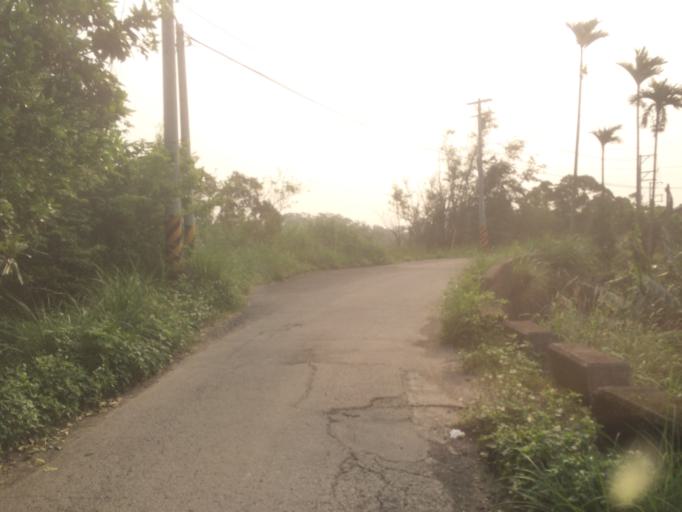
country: TW
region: Taiwan
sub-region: Hsinchu
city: Hsinchu
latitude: 24.7649
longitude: 120.9709
